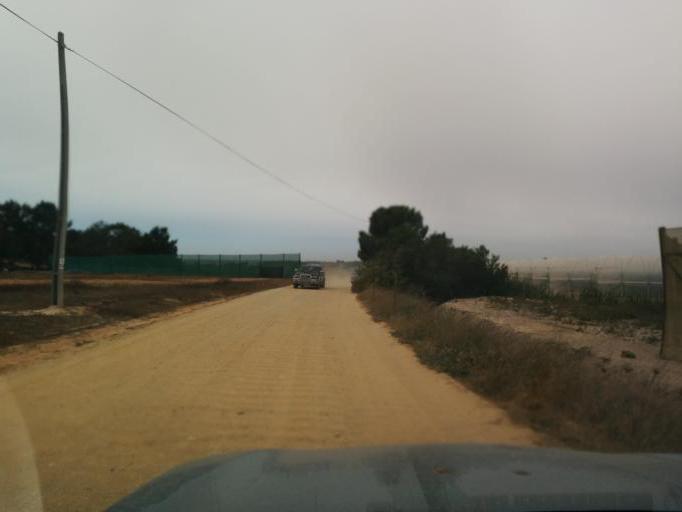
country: PT
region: Beja
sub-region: Odemira
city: Sao Teotonio
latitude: 37.5130
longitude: -8.7838
